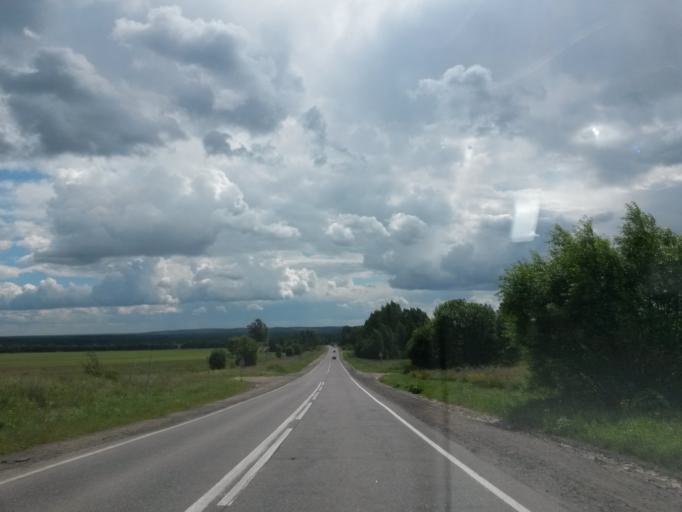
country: RU
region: Jaroslavl
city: Yaroslavl
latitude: 57.5416
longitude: 39.8640
